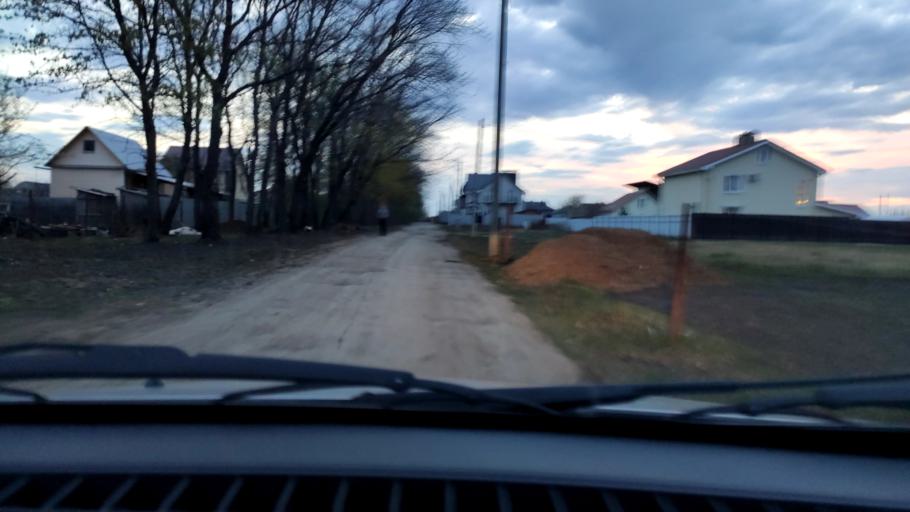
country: RU
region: Voronezj
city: Podgornoye
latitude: 51.7974
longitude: 39.2187
